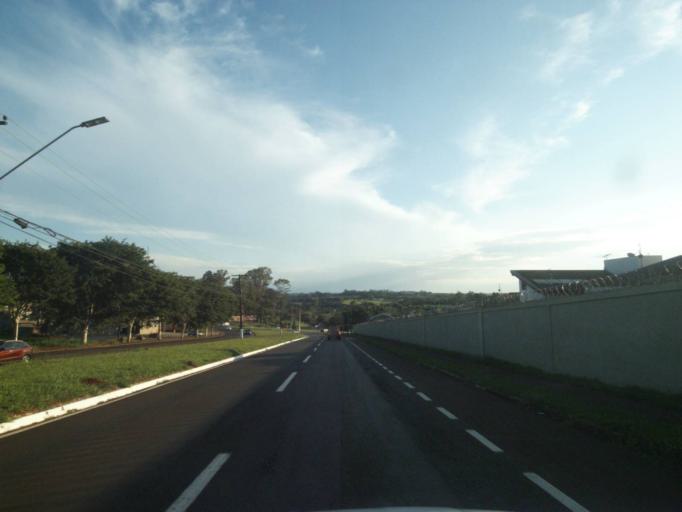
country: BR
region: Parana
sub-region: Londrina
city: Londrina
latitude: -23.3486
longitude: -51.1906
